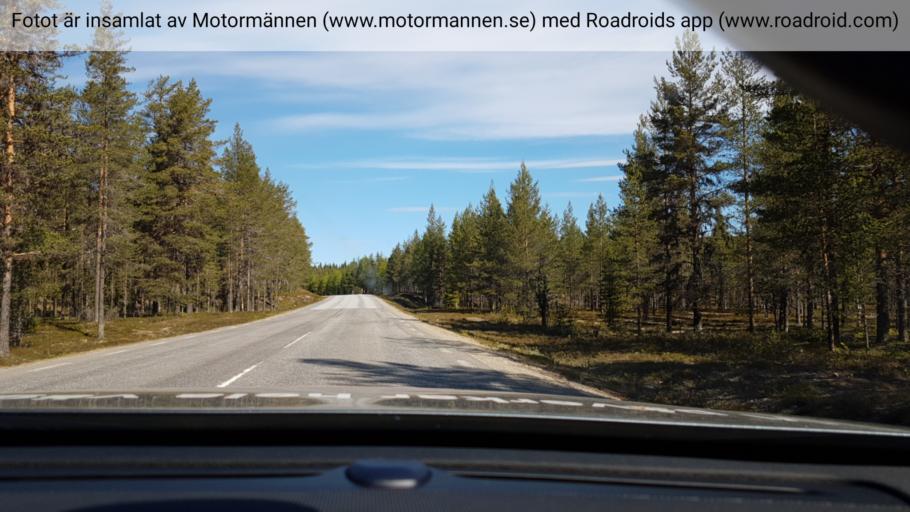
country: SE
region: Vaesterbotten
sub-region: Bjurholms Kommun
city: Bjurholm
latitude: 63.9949
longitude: 18.7933
